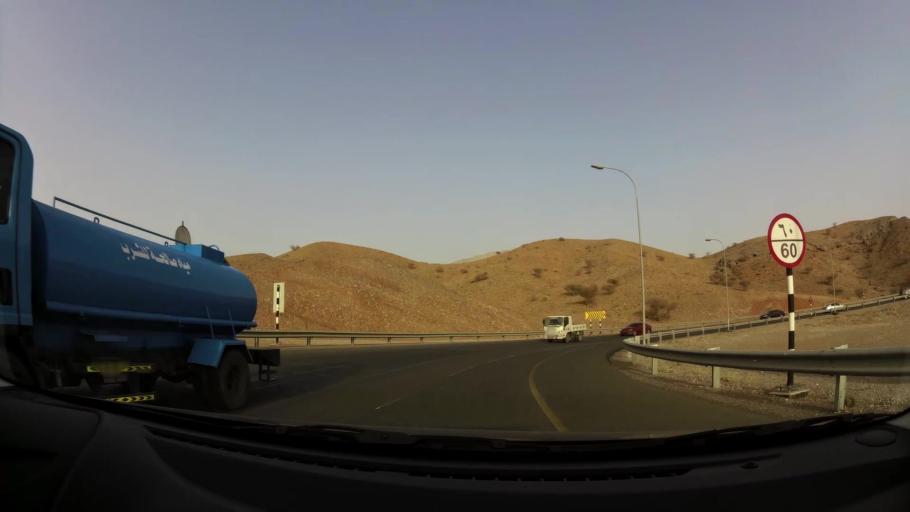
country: OM
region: Muhafazat Masqat
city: Bawshar
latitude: 23.5197
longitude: 58.3481
